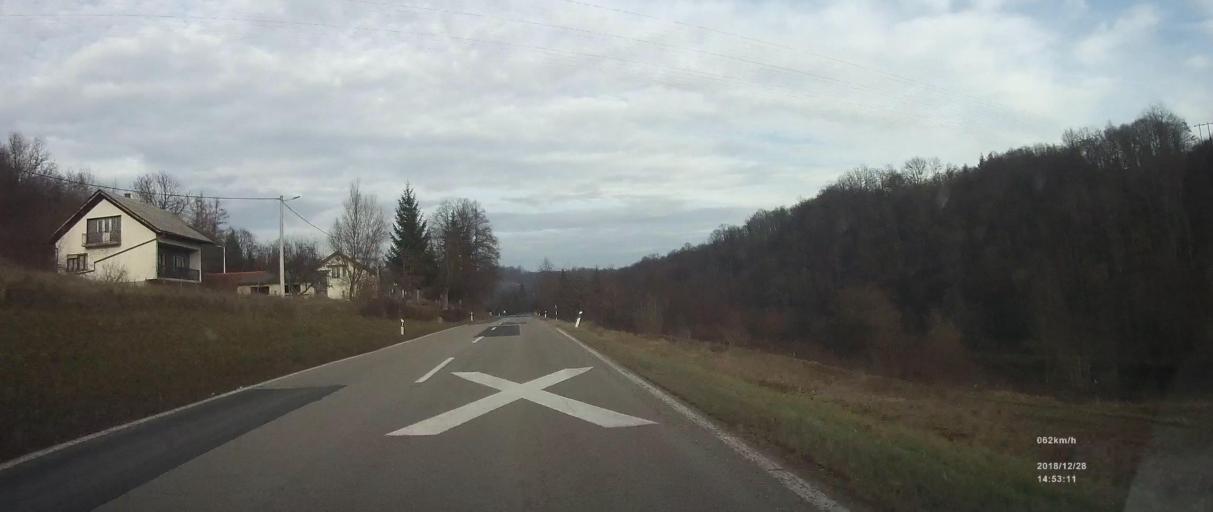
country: HR
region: Karlovacka
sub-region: Grad Karlovac
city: Karlovac
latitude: 45.4500
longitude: 15.4063
